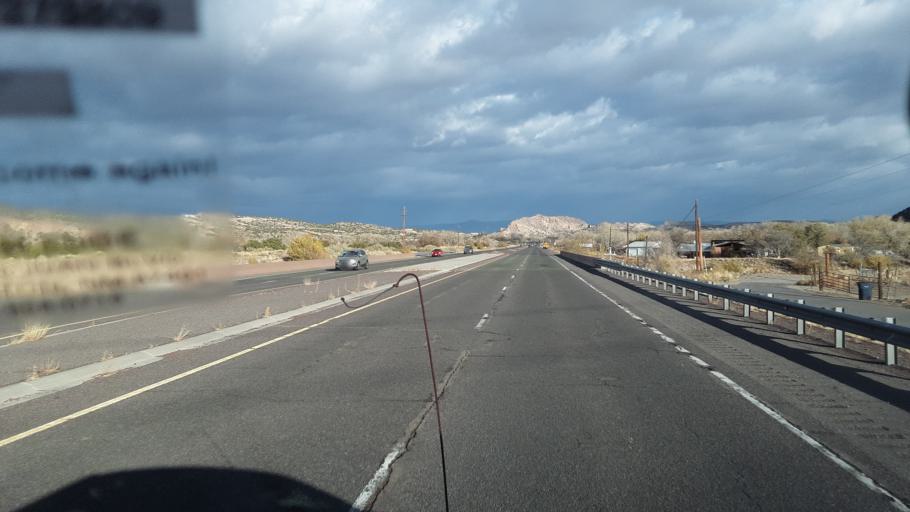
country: US
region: New Mexico
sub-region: Rio Arriba County
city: Ohkay Owingeh
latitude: 36.0805
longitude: -106.1291
